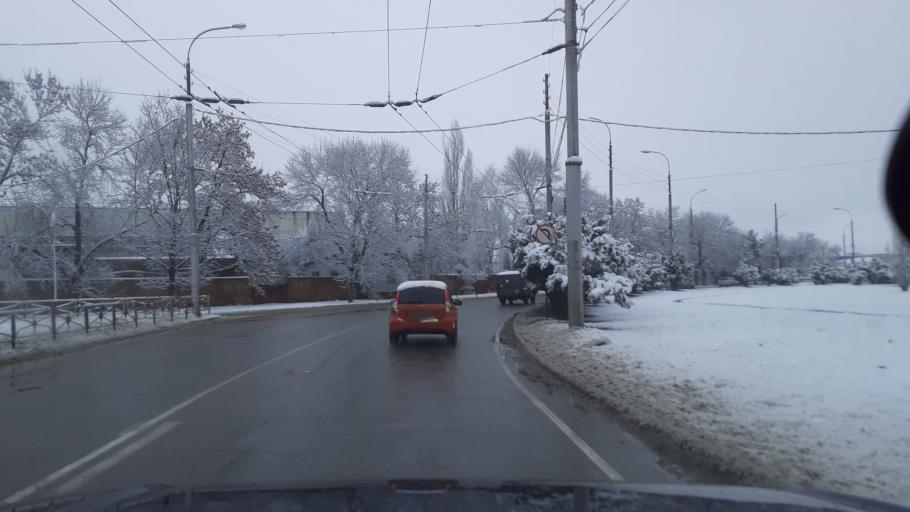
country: RU
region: Adygeya
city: Maykop
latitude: 44.5865
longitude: 40.1245
